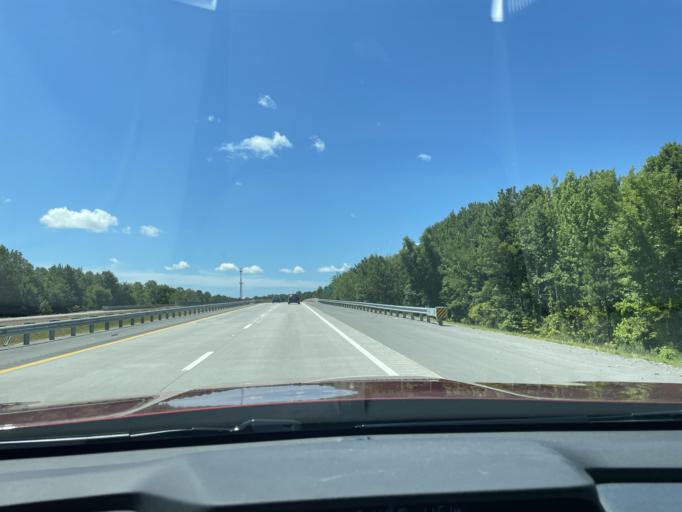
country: US
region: Arkansas
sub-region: Jefferson County
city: Sulphur Springs
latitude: 34.2072
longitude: -92.0721
